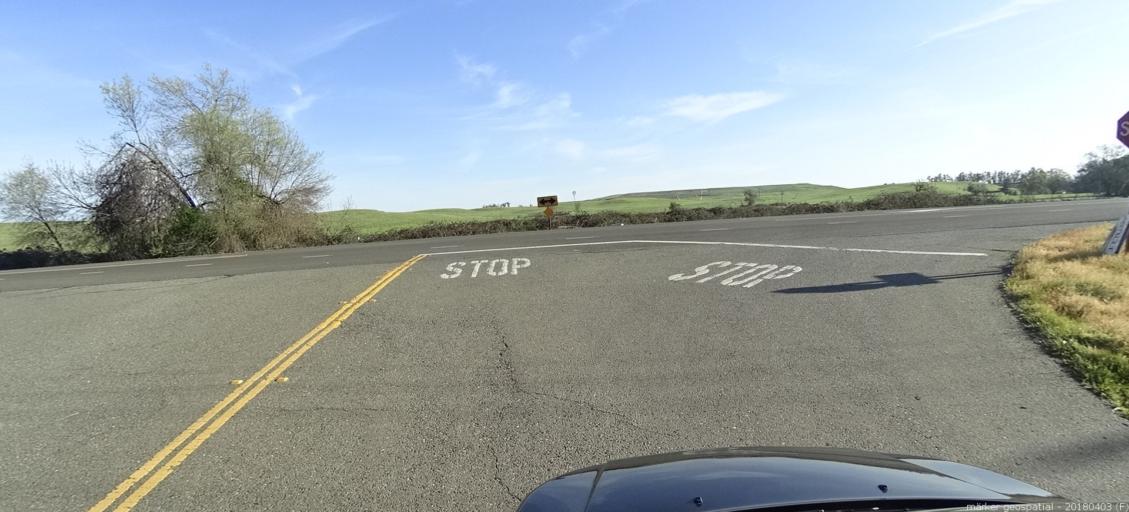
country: US
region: California
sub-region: Sacramento County
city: Rancho Murieta
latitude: 38.4968
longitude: -121.1969
